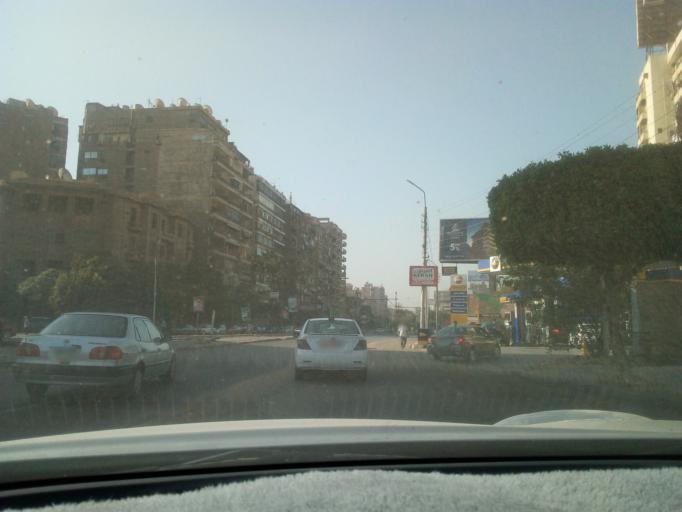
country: EG
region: Muhafazat al Qahirah
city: Cairo
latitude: 30.1001
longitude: 31.3238
